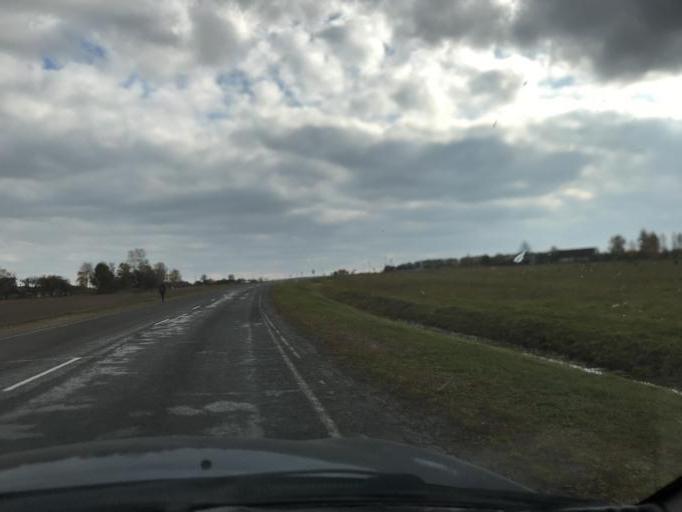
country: BY
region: Grodnenskaya
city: Lida
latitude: 53.7891
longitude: 25.1530
